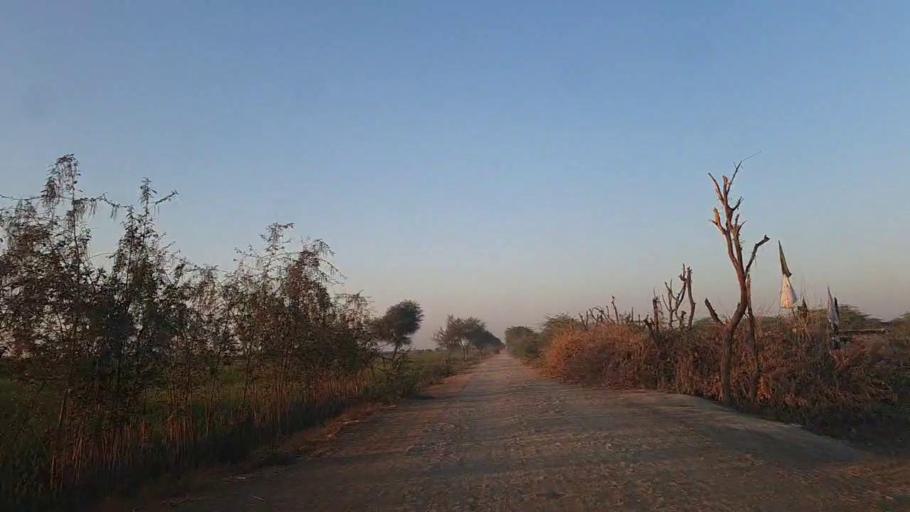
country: PK
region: Sindh
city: Naukot
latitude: 25.0514
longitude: 69.4070
